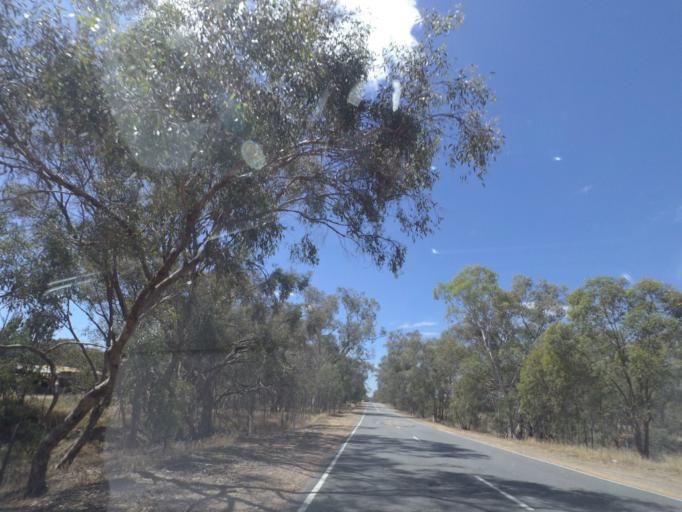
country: AU
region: Victoria
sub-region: Wangaratta
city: Wangaratta
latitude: -36.4462
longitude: 146.2416
